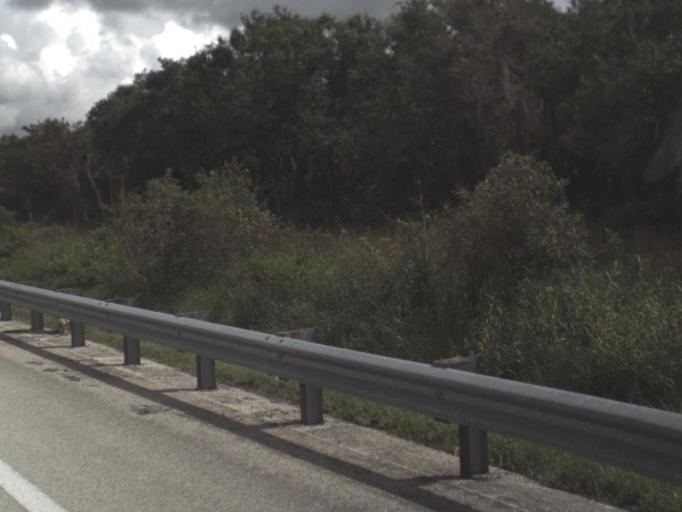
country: US
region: Florida
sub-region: Sarasota County
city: Warm Mineral Springs
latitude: 27.1953
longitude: -82.2010
